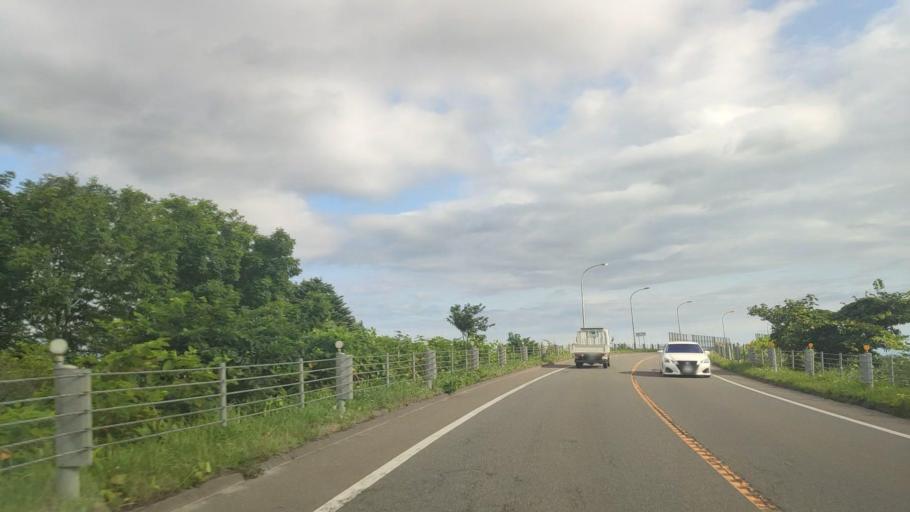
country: JP
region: Hokkaido
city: Niseko Town
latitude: 42.5812
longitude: 140.4541
